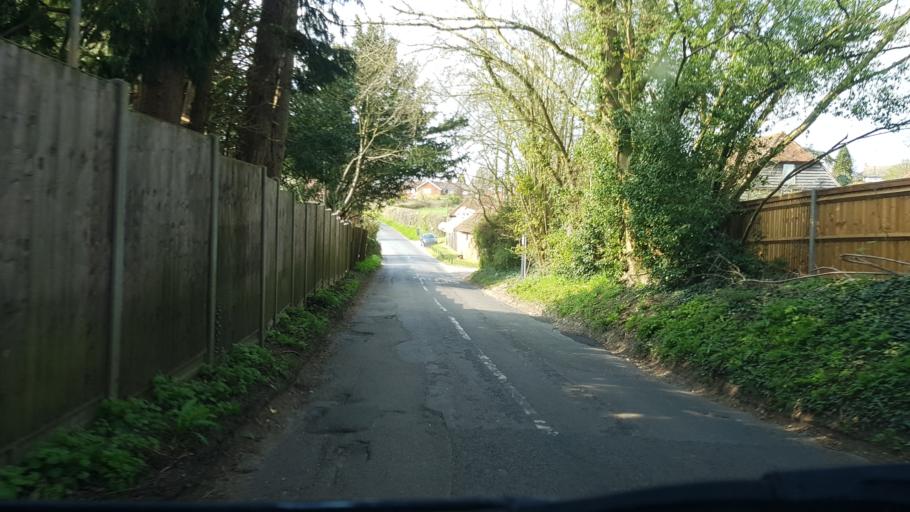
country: GB
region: England
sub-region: Surrey
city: Chilworth
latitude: 51.2334
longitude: -0.5403
